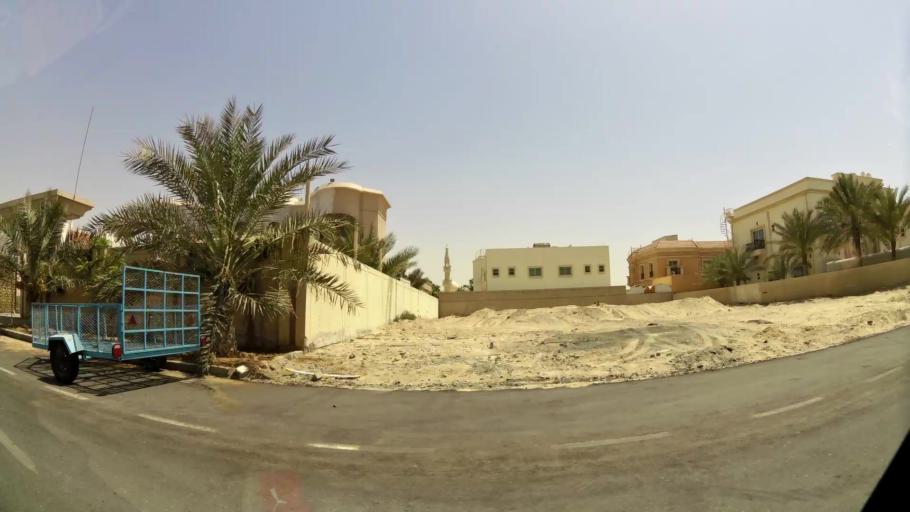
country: AE
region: Dubai
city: Dubai
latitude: 25.1035
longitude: 55.2232
